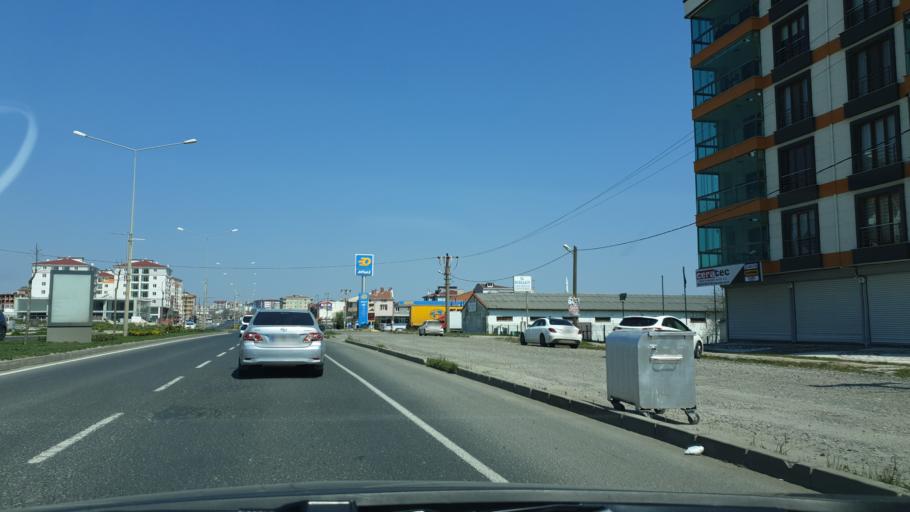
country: TR
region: Tekirdag
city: Corlu
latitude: 41.1543
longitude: 27.7809
